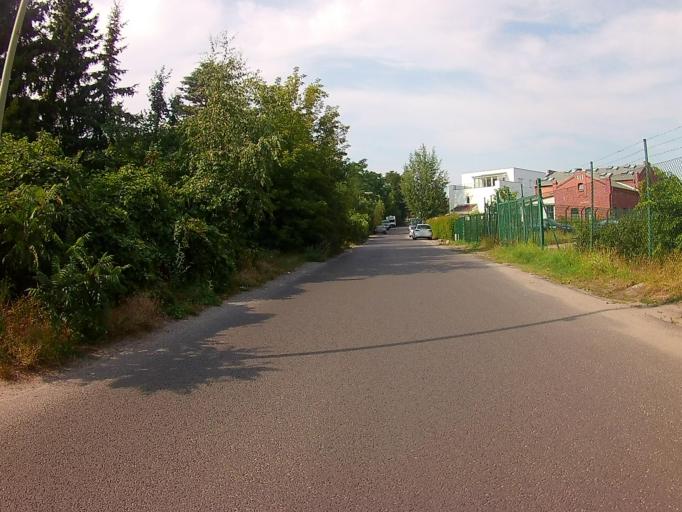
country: DE
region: Berlin
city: Grunau
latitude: 52.4263
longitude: 13.5722
